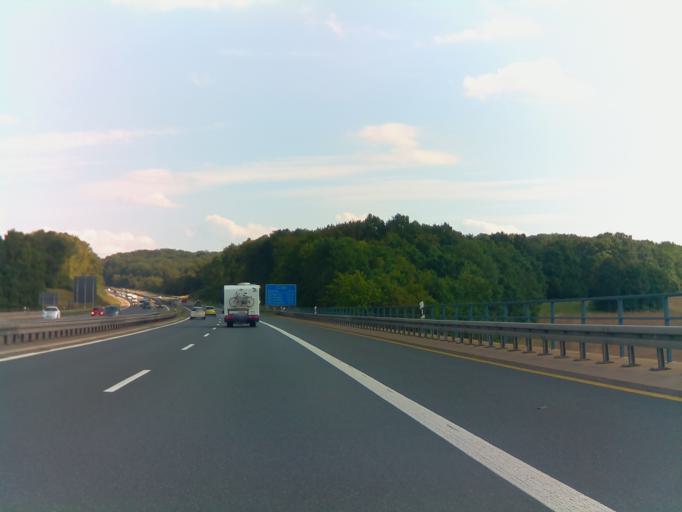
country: DE
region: Bavaria
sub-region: Regierungsbezirk Unterfranken
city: Oberthulba
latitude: 50.1912
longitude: 9.9429
